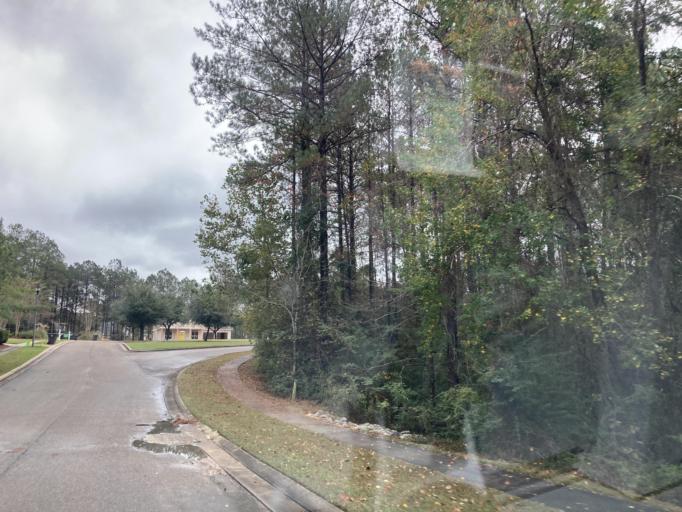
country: US
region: Mississippi
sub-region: Lamar County
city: West Hattiesburg
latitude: 31.2876
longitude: -89.4757
